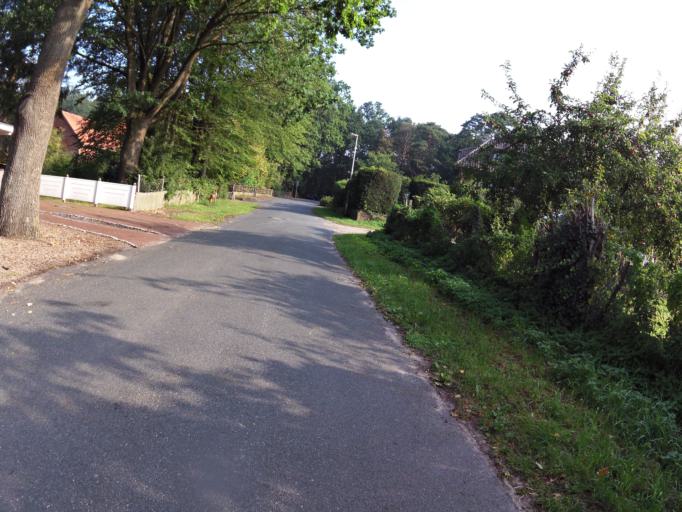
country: DE
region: Lower Saxony
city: Verden
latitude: 52.9416
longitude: 9.2273
